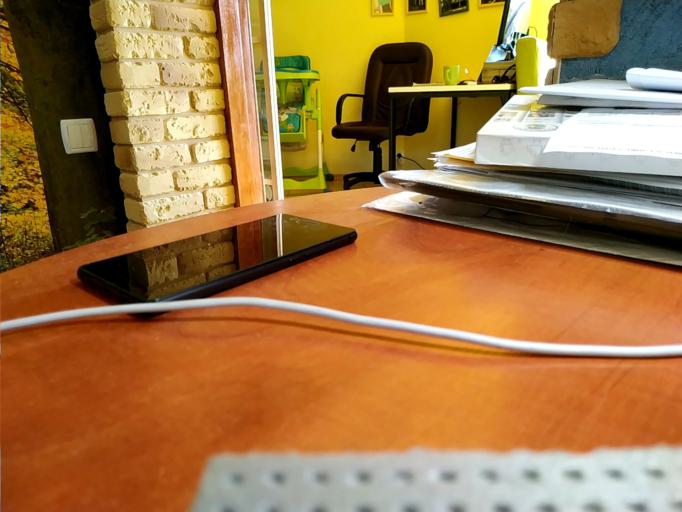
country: RU
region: Tverskaya
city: Likhoslavl'
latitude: 57.3647
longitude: 35.4498
